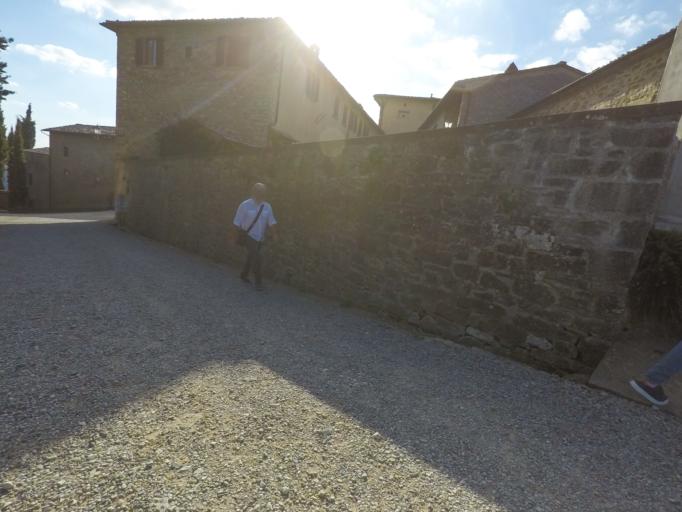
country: IT
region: Tuscany
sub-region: Provincia di Siena
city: Radda in Chianti
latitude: 43.5195
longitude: 11.4033
